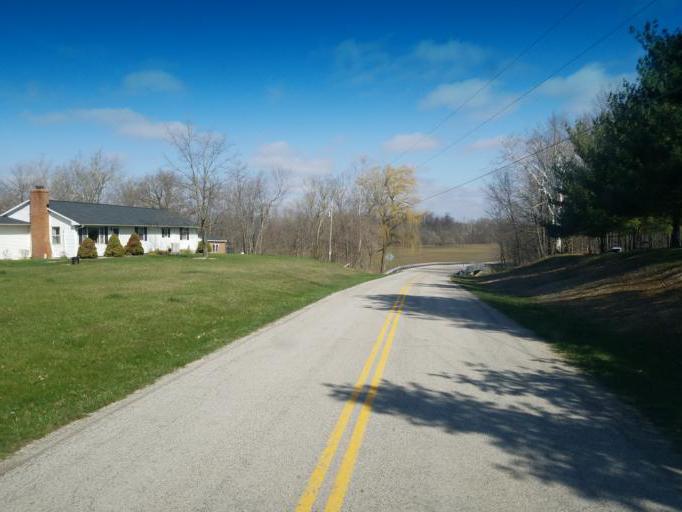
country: US
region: Ohio
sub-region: Crawford County
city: Bucyrus
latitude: 40.8350
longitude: -82.8727
